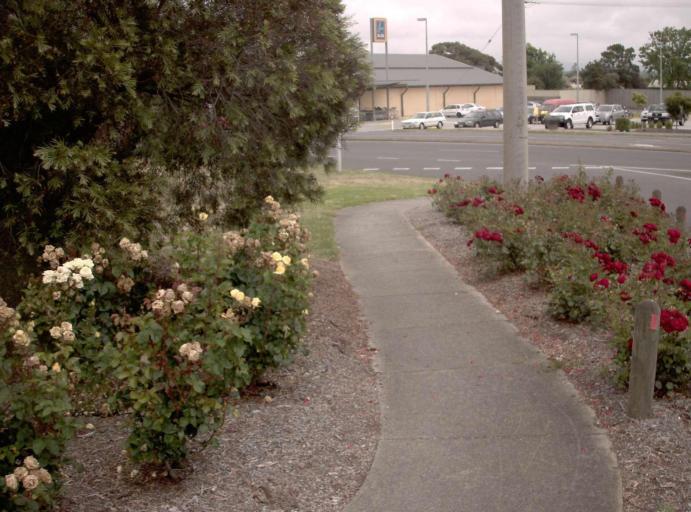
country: AU
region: Victoria
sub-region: Latrobe
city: Morwell
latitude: -38.2388
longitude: 146.4045
